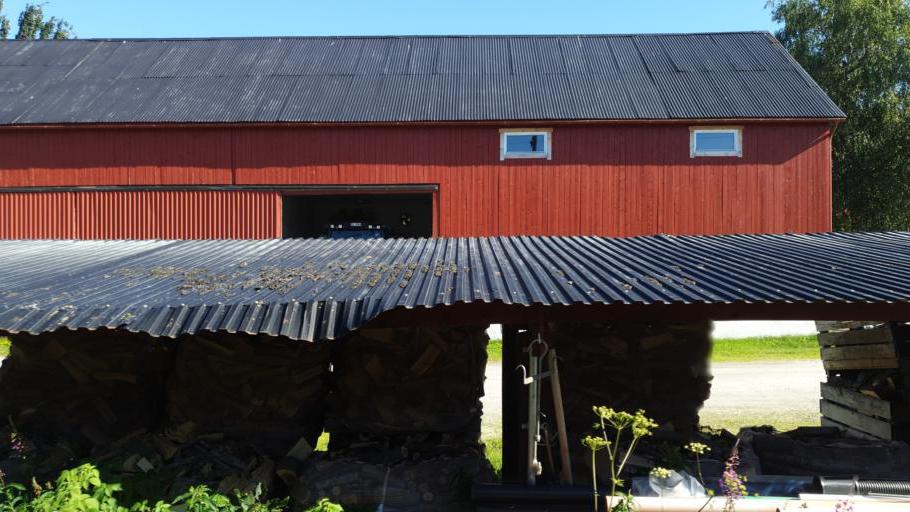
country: NO
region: Sor-Trondelag
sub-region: Orkdal
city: Orkanger
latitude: 63.2830
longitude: 9.8360
